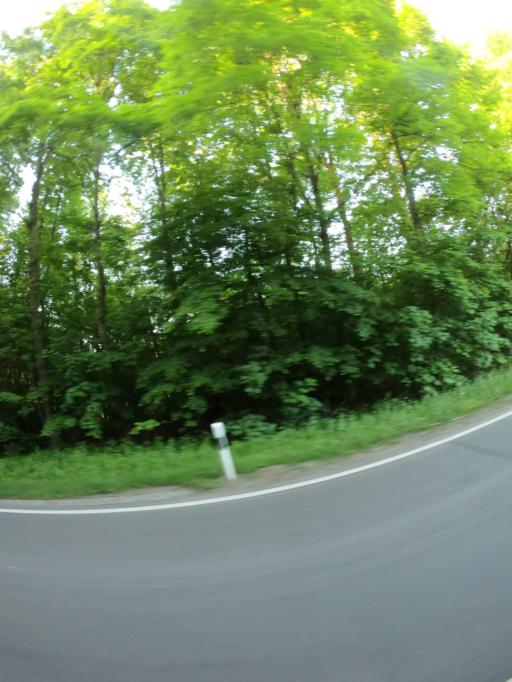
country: DE
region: Bavaria
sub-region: Upper Bavaria
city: Inning am Holz
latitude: 48.3372
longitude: 12.0360
